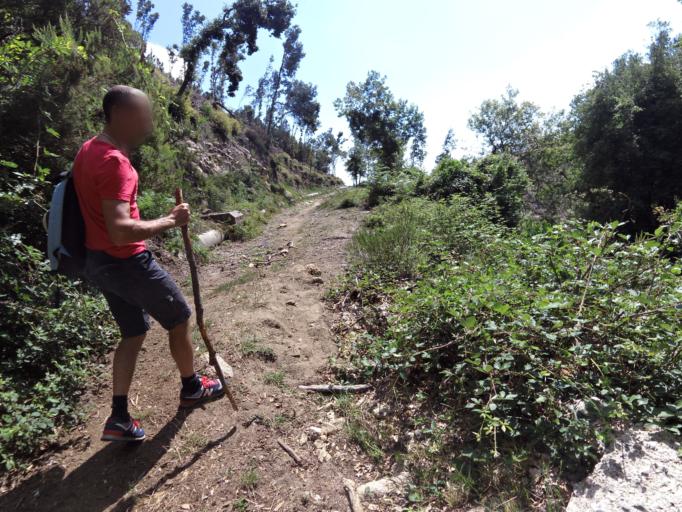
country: IT
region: Calabria
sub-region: Provincia di Vibo-Valentia
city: Nardodipace
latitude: 38.5072
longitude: 16.3891
